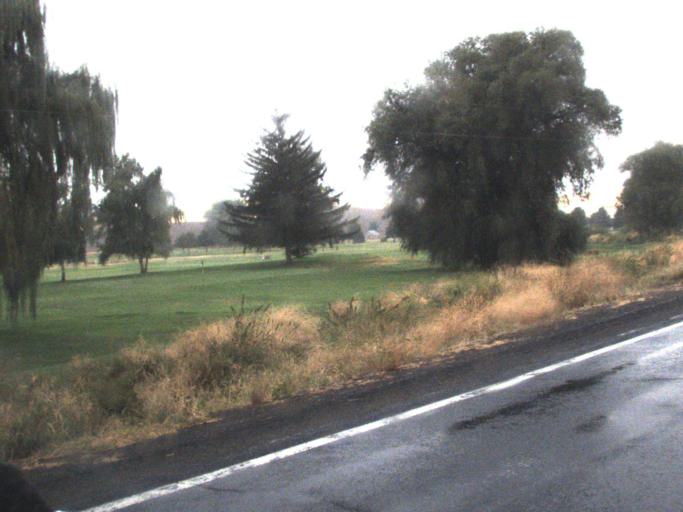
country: US
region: Washington
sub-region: Whitman County
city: Colfax
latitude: 47.0944
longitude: -117.5919
